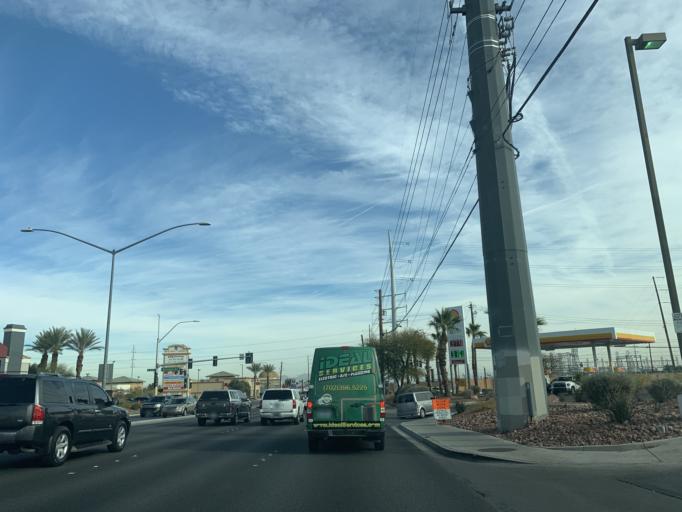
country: US
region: Nevada
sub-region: Clark County
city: Spring Valley
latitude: 36.1590
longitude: -115.2814
